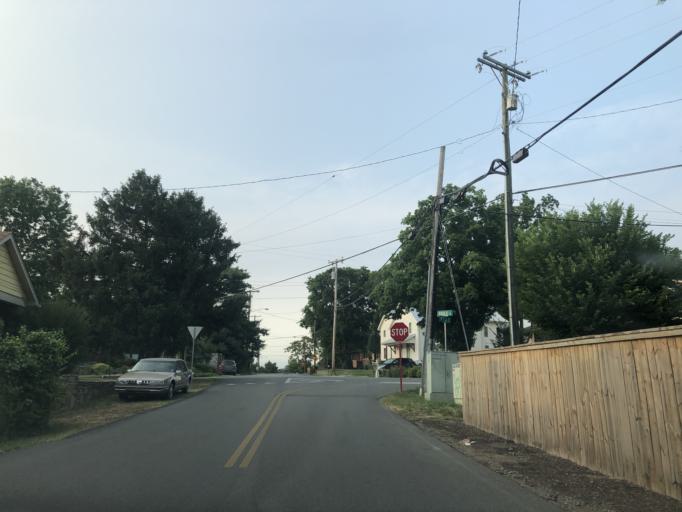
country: US
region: Tennessee
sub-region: Davidson County
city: Oak Hill
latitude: 36.1261
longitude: -86.7833
